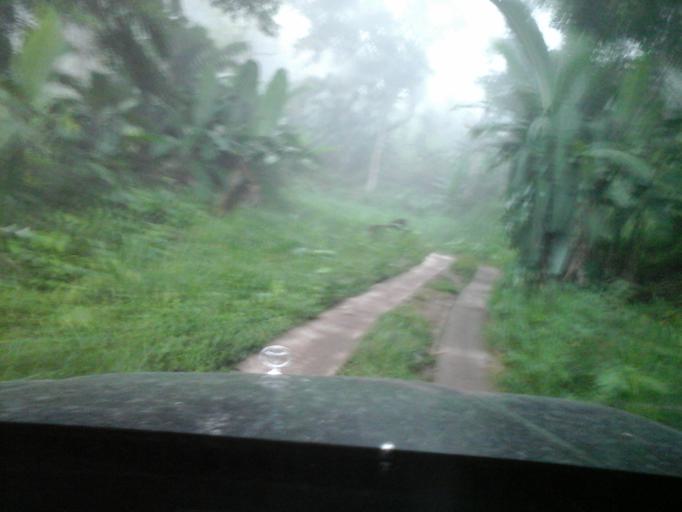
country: CO
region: Cesar
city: Agustin Codazzi
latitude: 9.9423
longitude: -73.1243
